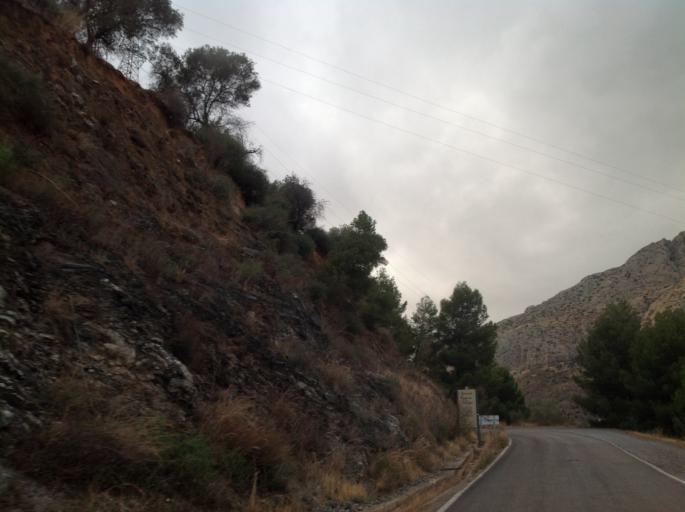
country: ES
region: Andalusia
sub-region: Provincia de Malaga
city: Carratraca
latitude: 36.9050
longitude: -4.7616
